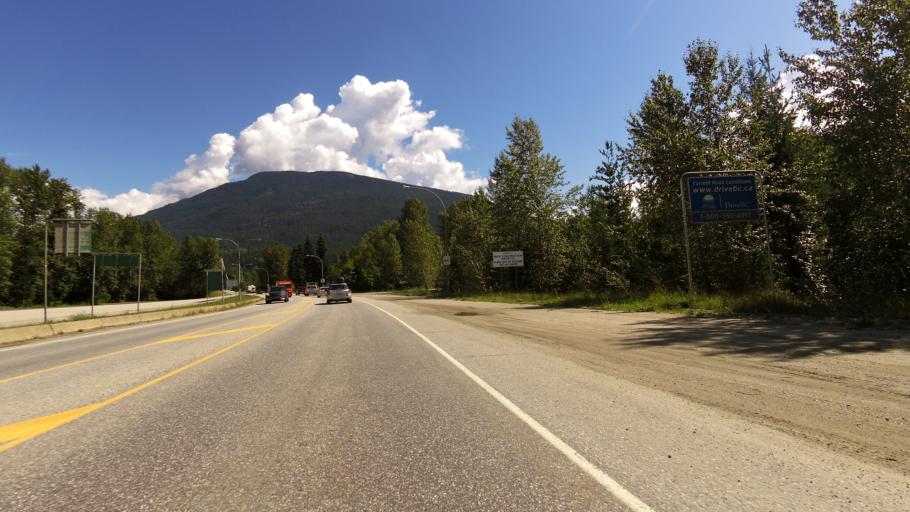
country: CA
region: British Columbia
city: Revelstoke
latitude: 51.0035
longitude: -118.2243
